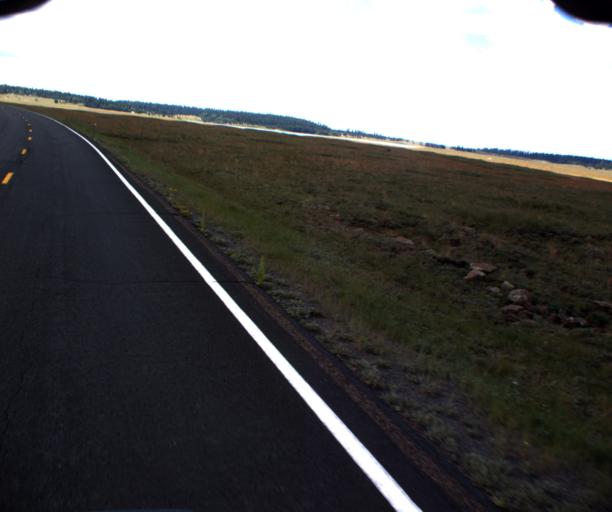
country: US
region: Arizona
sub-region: Apache County
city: Eagar
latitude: 33.8996
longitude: -109.4133
